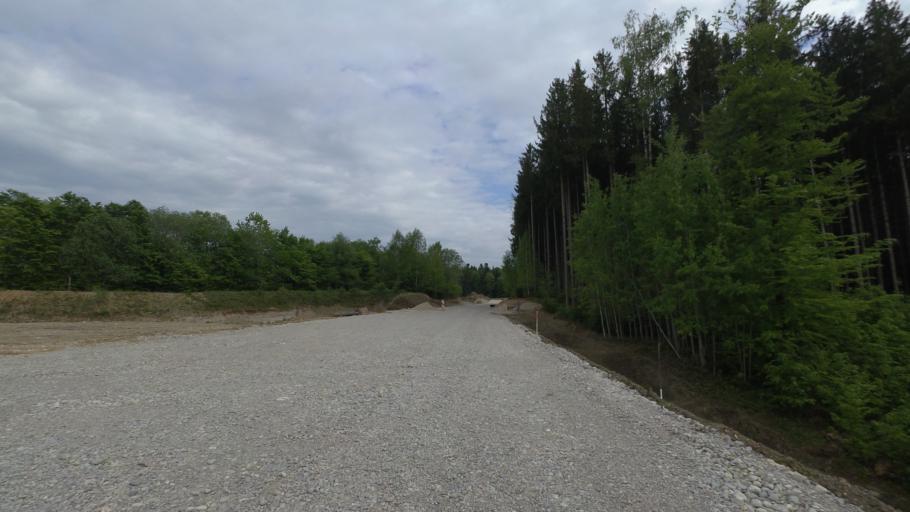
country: DE
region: Bavaria
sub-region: Upper Bavaria
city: Nussdorf
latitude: 47.8996
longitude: 12.6182
